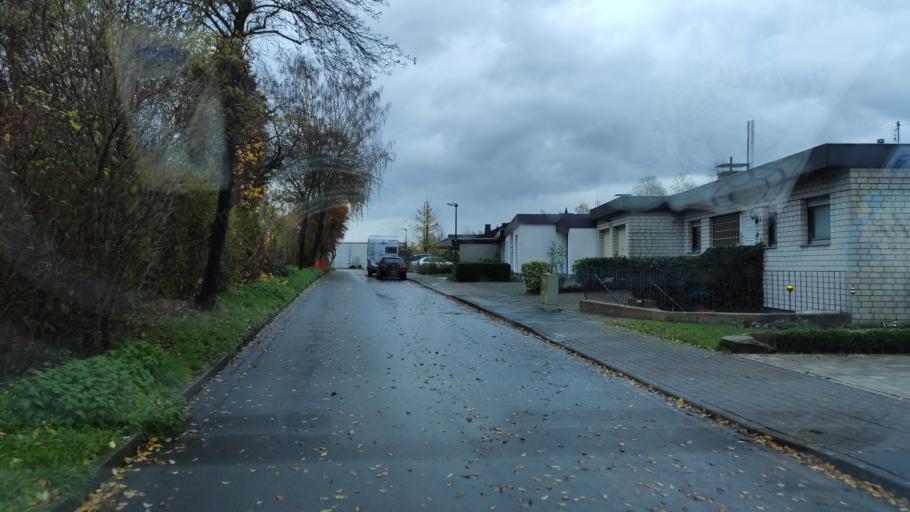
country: DE
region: North Rhine-Westphalia
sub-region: Regierungsbezirk Detmold
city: Hoexter
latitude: 51.7859
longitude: 9.3843
